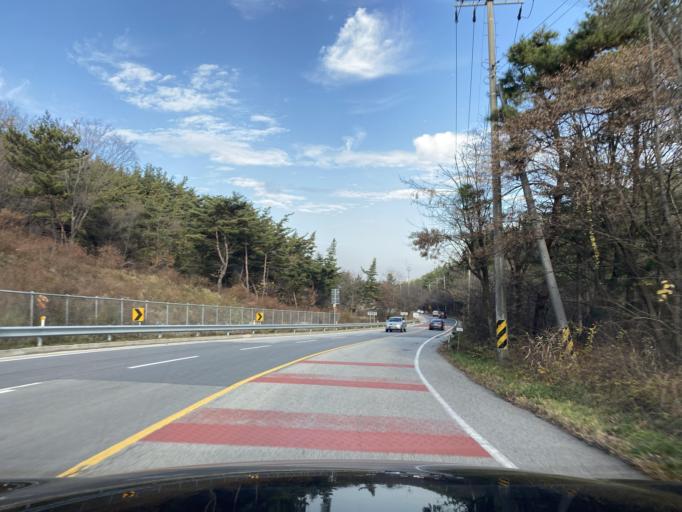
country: KR
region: Chungcheongnam-do
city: Hongsung
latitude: 36.6689
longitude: 126.6386
